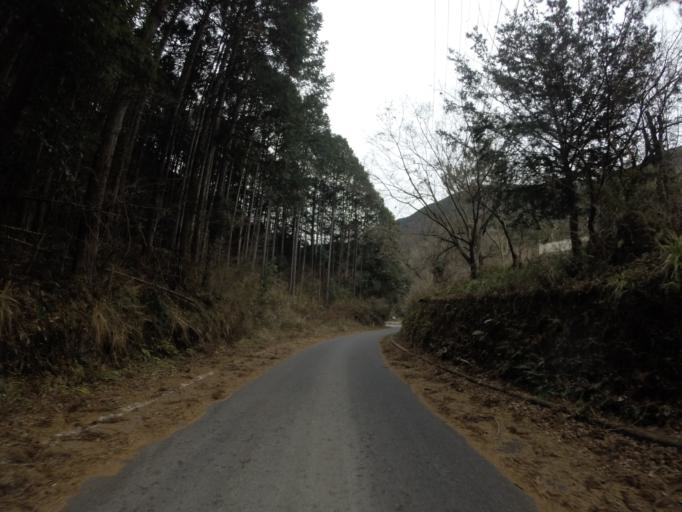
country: JP
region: Shizuoka
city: Fujinomiya
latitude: 35.2765
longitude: 138.5310
